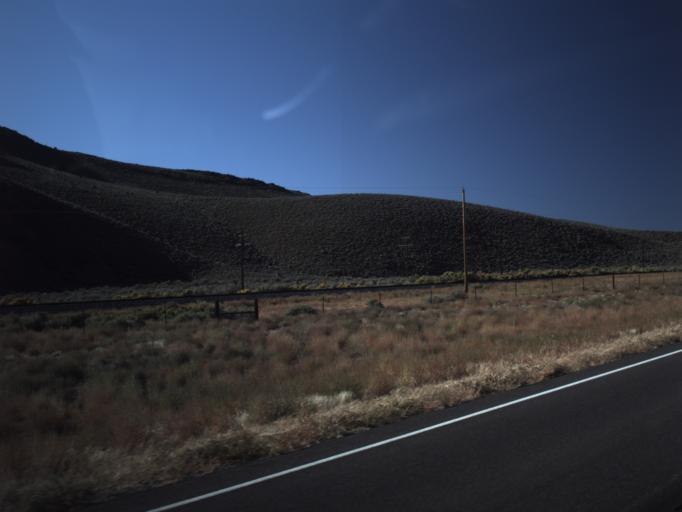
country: US
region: Utah
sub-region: Washington County
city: Enterprise
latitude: 37.7816
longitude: -113.9655
